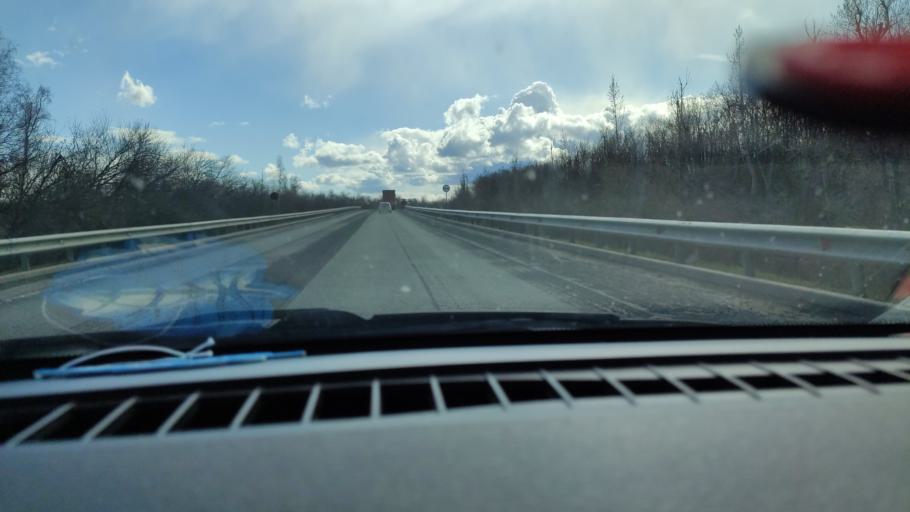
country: RU
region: Saratov
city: Dukhovnitskoye
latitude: 52.6247
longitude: 48.1782
